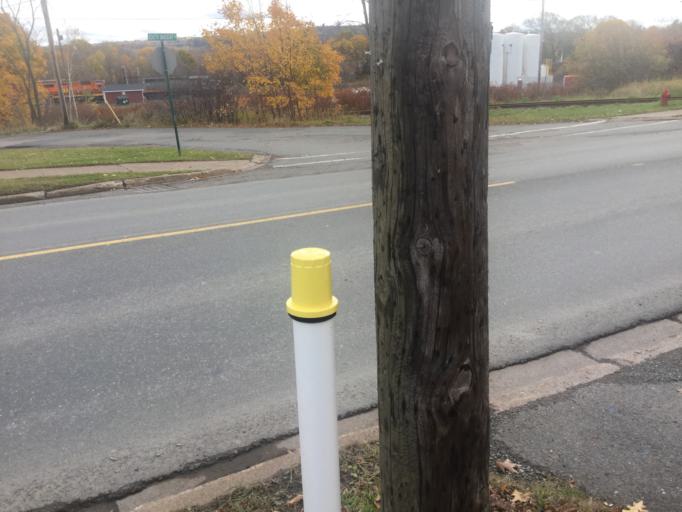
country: CA
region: Nova Scotia
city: New Glasgow
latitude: 45.5554
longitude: -62.6610
